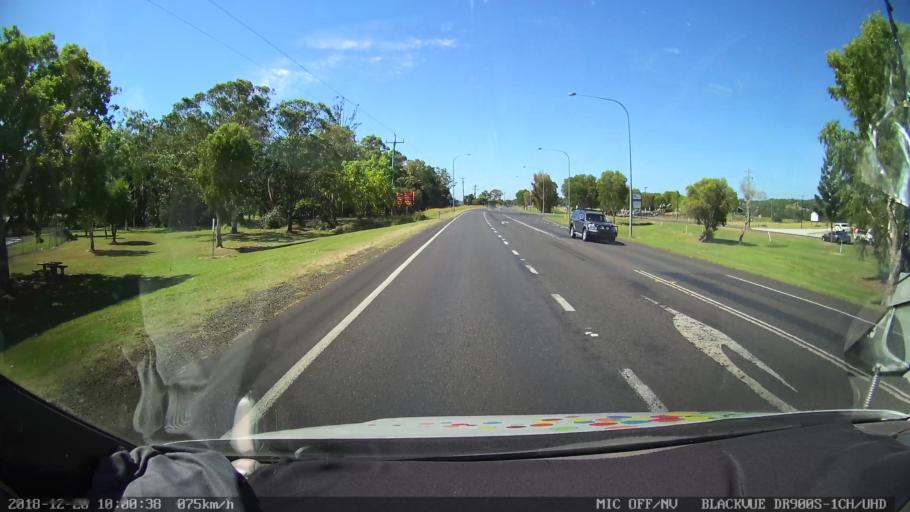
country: AU
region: New South Wales
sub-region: Lismore Municipality
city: Lismore
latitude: -28.8347
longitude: 153.2647
